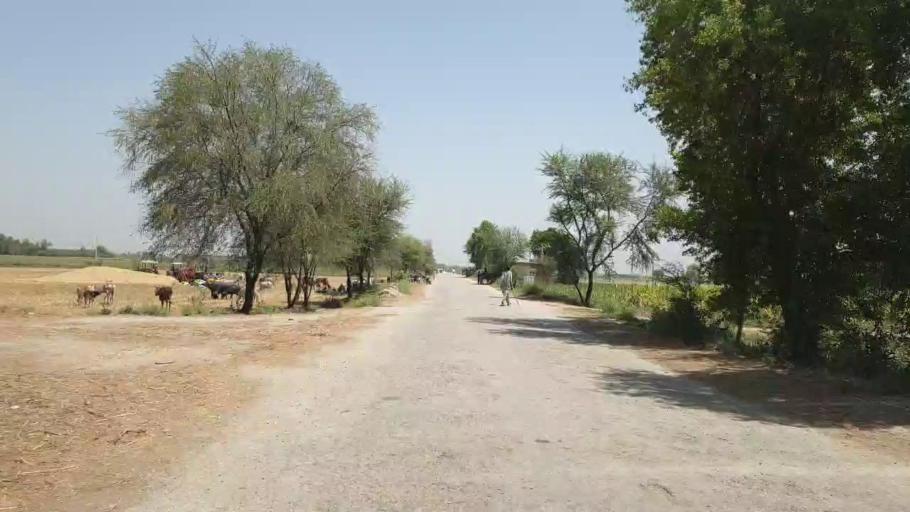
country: PK
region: Sindh
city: Adilpur
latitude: 27.8759
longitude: 69.2858
